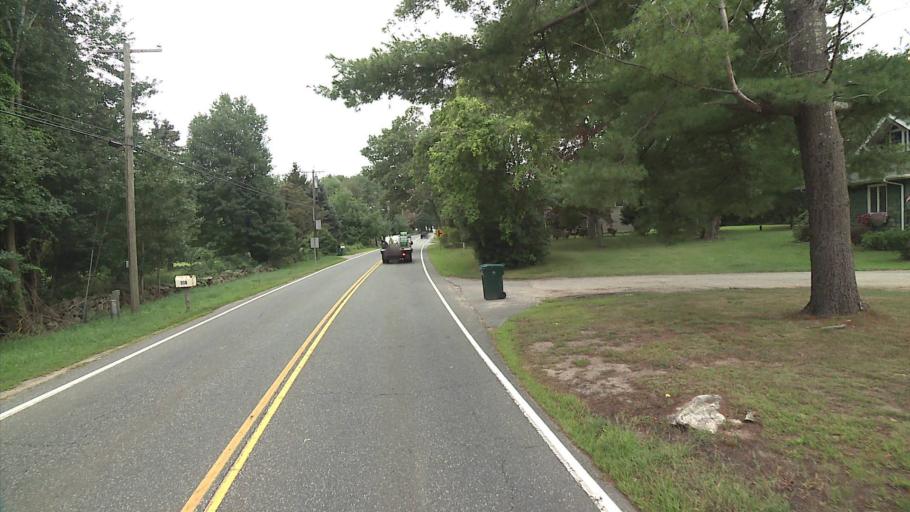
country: US
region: Connecticut
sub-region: New London County
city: Niantic
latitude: 41.2905
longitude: -72.2701
